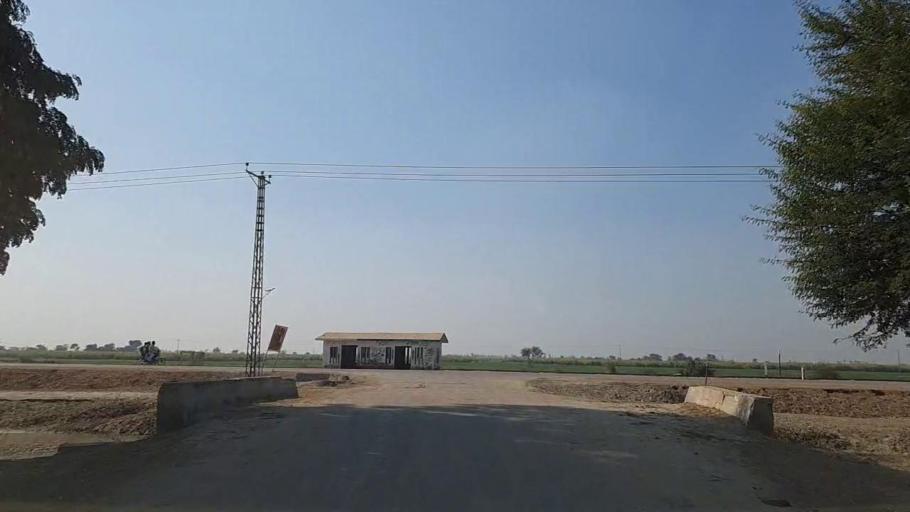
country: PK
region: Sindh
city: Daur
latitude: 26.5020
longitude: 68.3101
